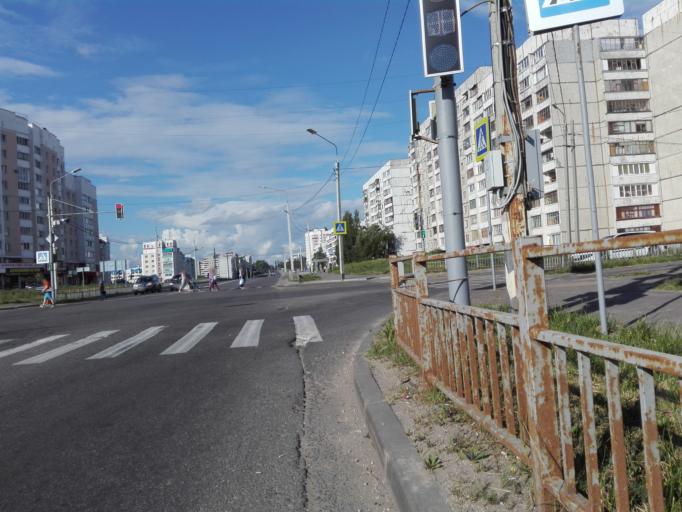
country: RU
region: Orjol
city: Orel
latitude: 53.0101
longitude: 36.1256
